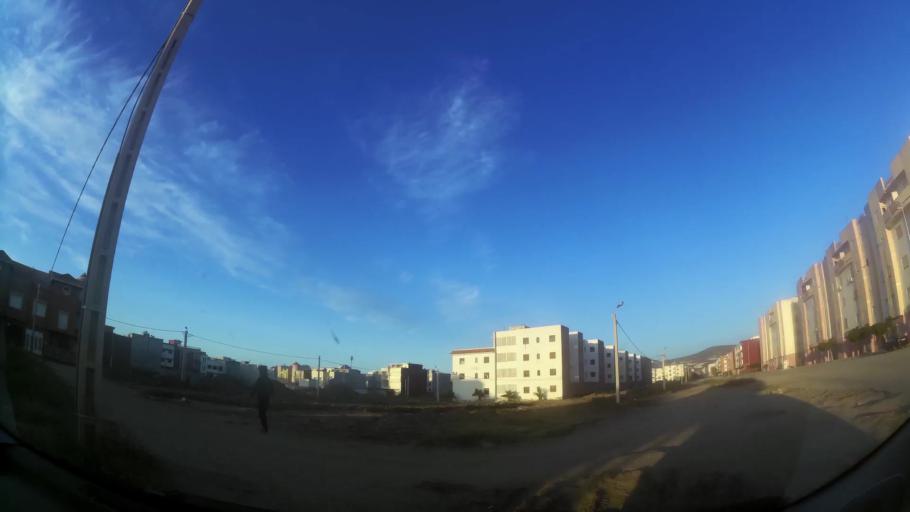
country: MA
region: Oriental
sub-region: Berkane-Taourirt
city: Madagh
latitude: 35.0779
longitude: -2.2336
